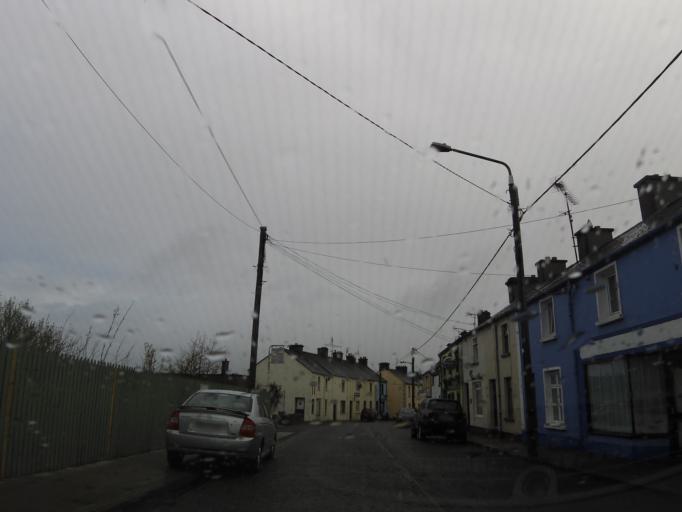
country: IE
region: Connaught
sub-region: Sligo
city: Collooney
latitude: 54.1846
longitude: -8.4925
